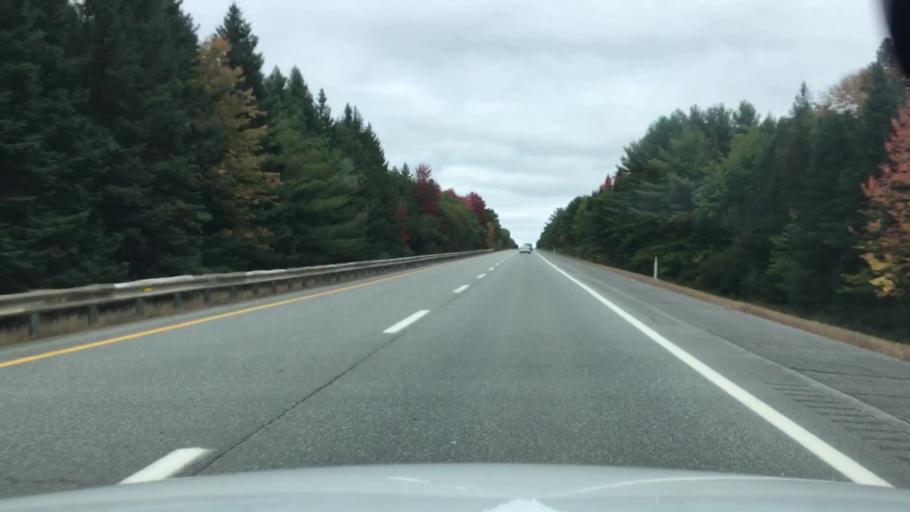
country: US
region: Maine
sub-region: Penobscot County
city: Plymouth
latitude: 44.7905
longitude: -69.1937
